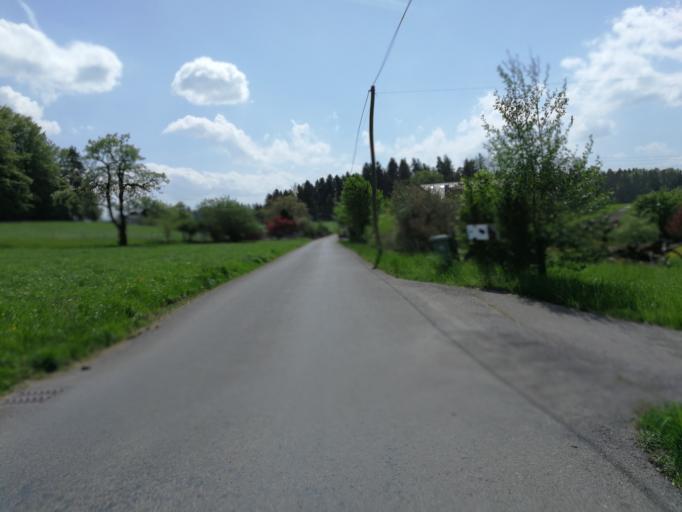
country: CH
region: Zurich
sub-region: Bezirk Hinwil
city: Binzikon
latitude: 47.2837
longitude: 8.7466
